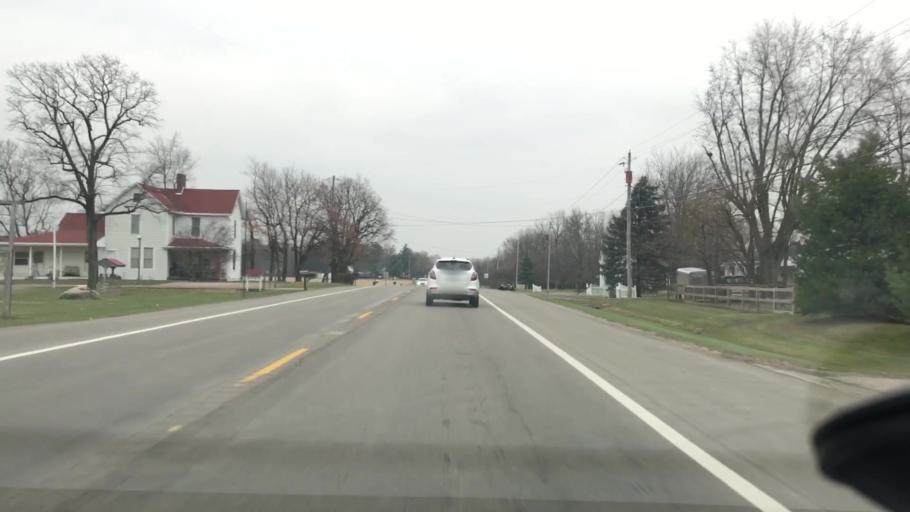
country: US
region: Ohio
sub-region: Greene County
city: Yellow Springs
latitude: 39.8430
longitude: -83.8617
